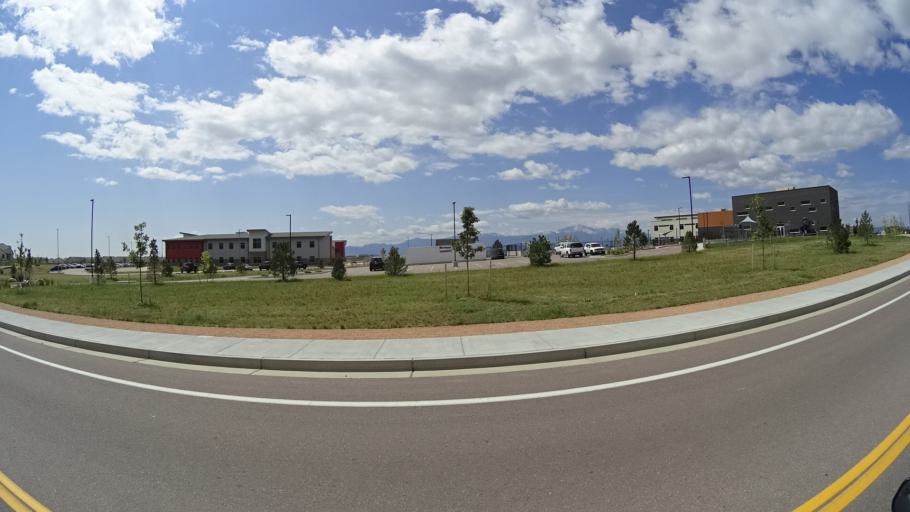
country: US
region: Colorado
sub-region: El Paso County
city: Cimarron Hills
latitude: 38.9325
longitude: -104.6580
